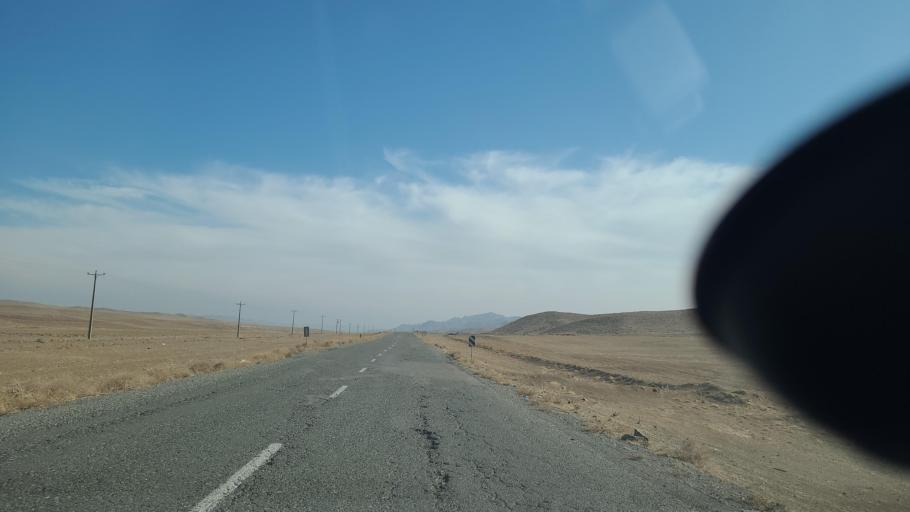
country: IR
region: Razavi Khorasan
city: Fariman
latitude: 35.5906
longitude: 59.6117
